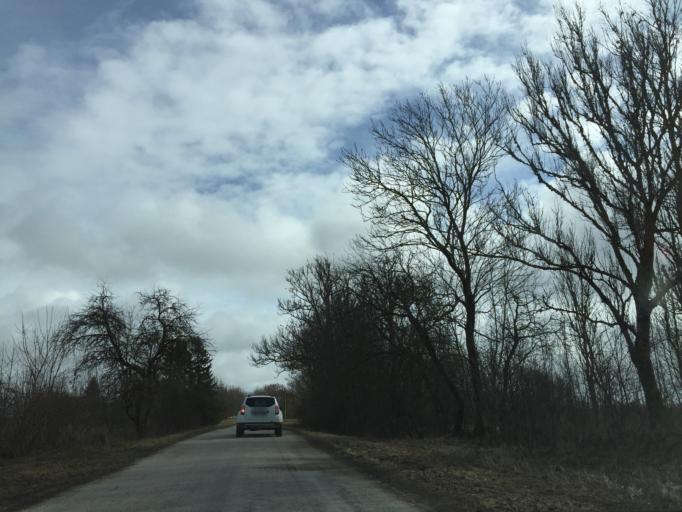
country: EE
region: Laeaene
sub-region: Lihula vald
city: Lihula
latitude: 58.7368
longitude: 23.8352
